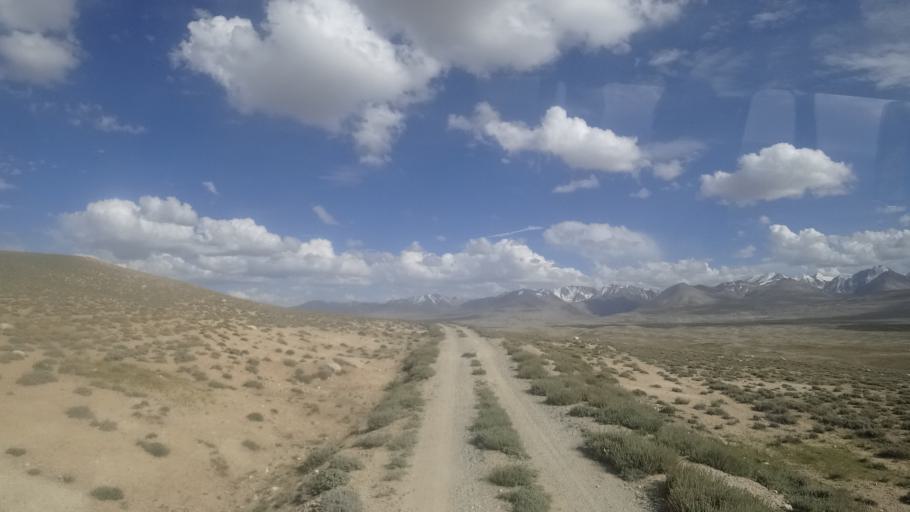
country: TJ
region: Gorno-Badakhshan
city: Murghob
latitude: 37.4696
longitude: 73.5435
